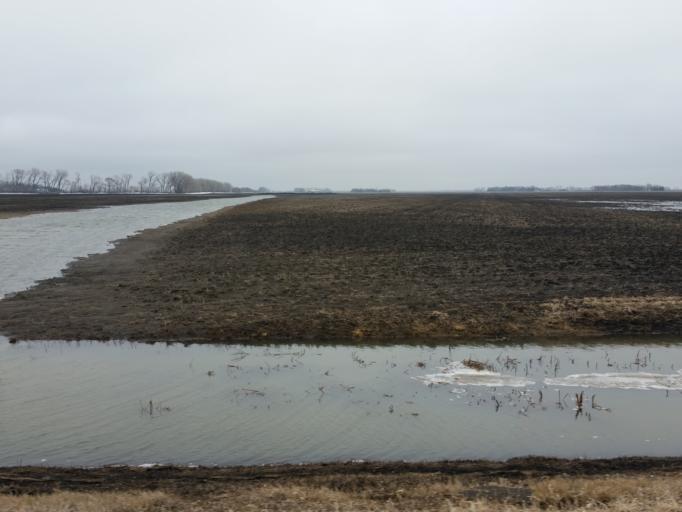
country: US
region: North Dakota
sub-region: Walsh County
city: Grafton
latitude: 48.3831
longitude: -97.2210
